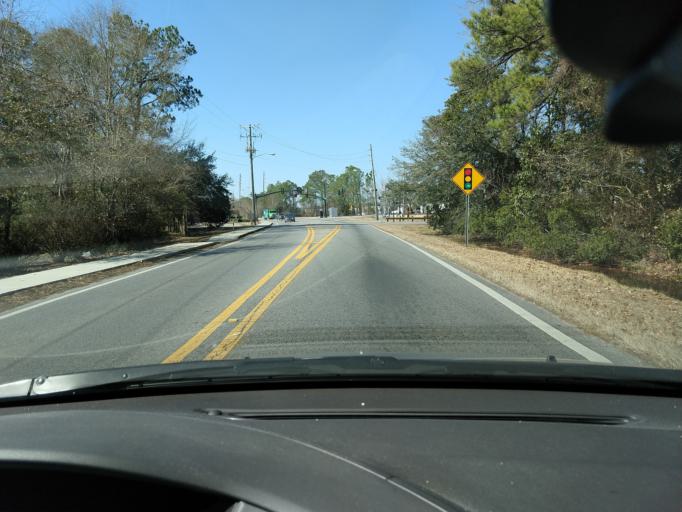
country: US
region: Mississippi
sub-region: Jackson County
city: Gulf Park Estates
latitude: 30.4100
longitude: -88.7849
